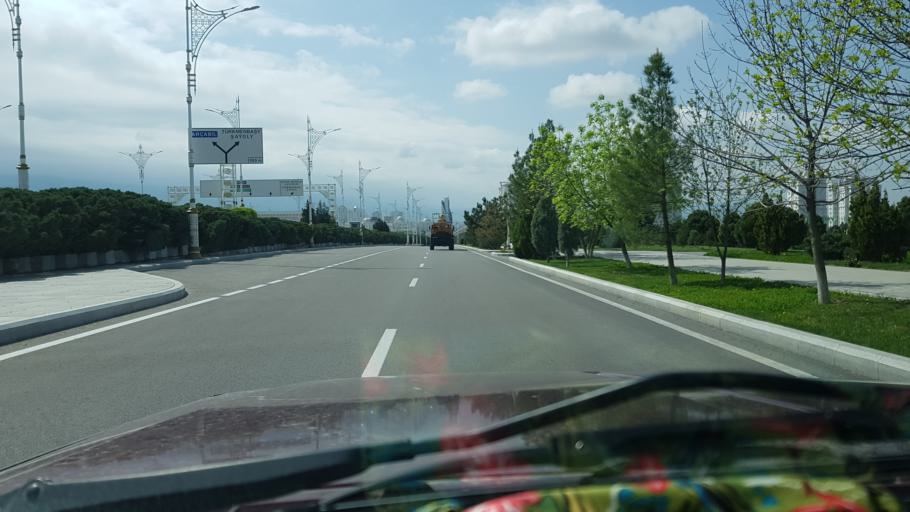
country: TM
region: Ahal
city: Ashgabat
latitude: 37.8795
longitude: 58.3845
